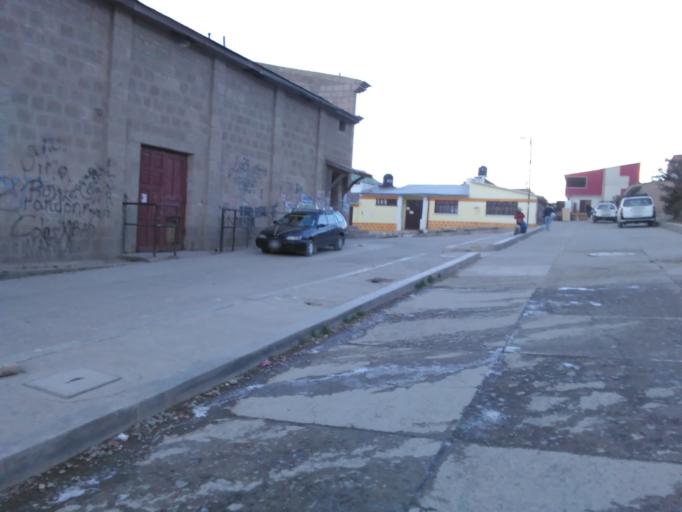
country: BO
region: Potosi
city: Llallagua
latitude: -18.4221
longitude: -66.5908
